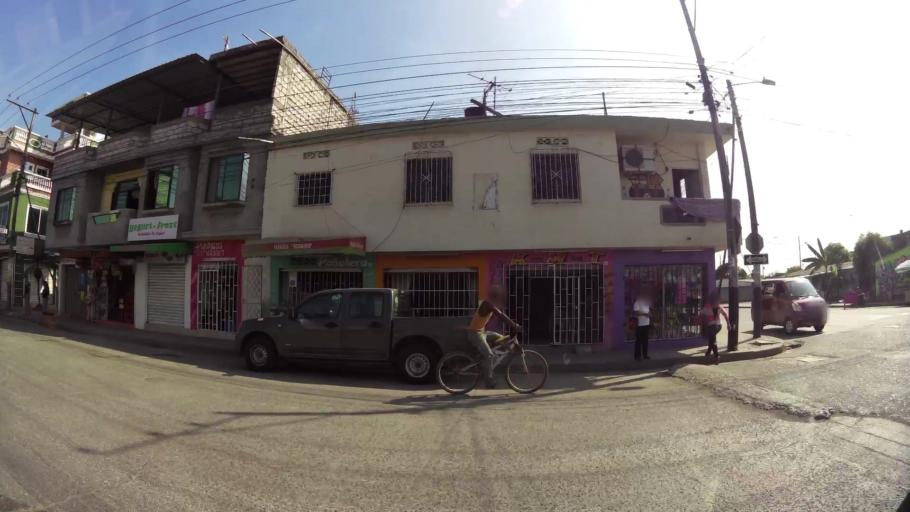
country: EC
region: Guayas
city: Eloy Alfaro
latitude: -2.1687
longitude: -79.7977
